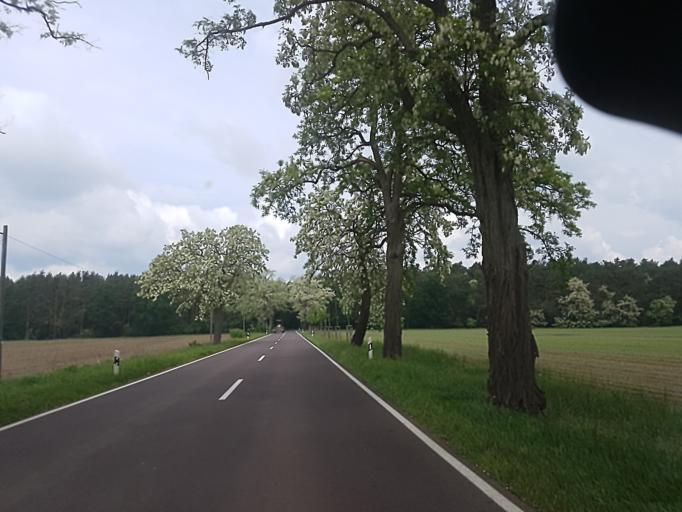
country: DE
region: Saxony-Anhalt
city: Lindau
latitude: 52.0869
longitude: 12.2250
